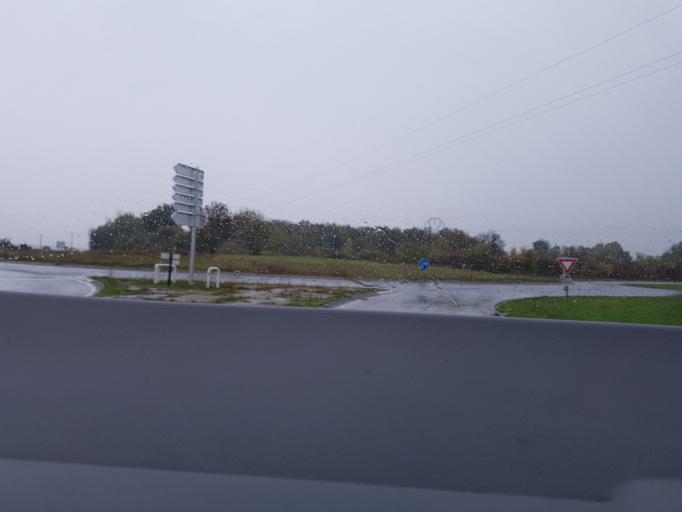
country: FR
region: Aquitaine
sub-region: Departement de la Gironde
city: Saint-Louis-de-Montferrand
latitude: 44.9599
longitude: -0.5181
